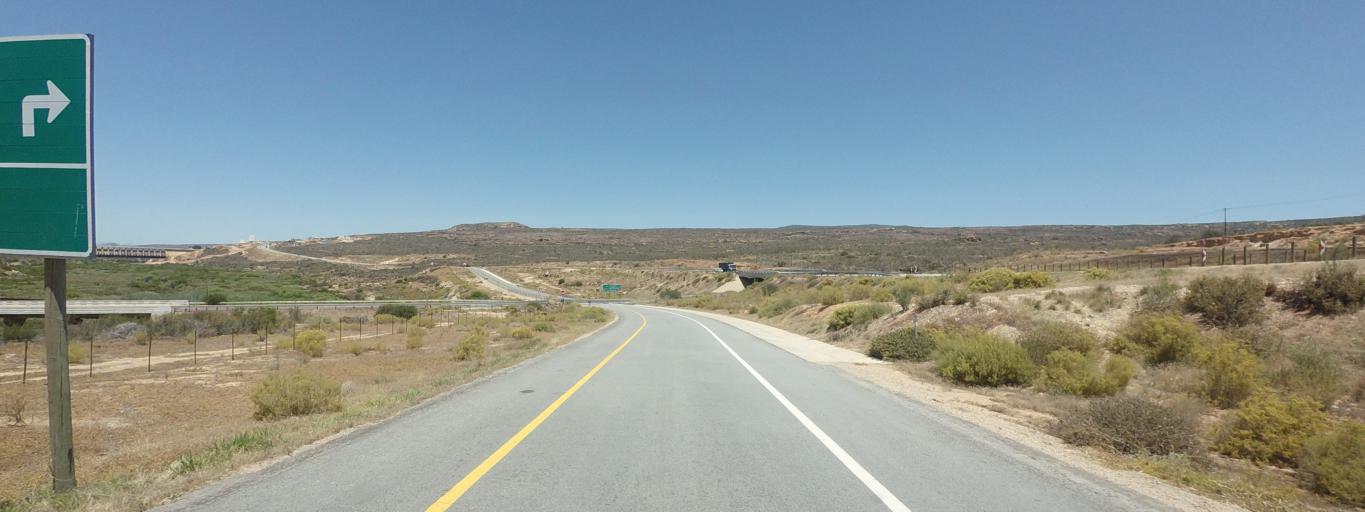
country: ZA
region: Western Cape
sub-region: West Coast District Municipality
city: Clanwilliam
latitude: -32.1718
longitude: 18.8686
